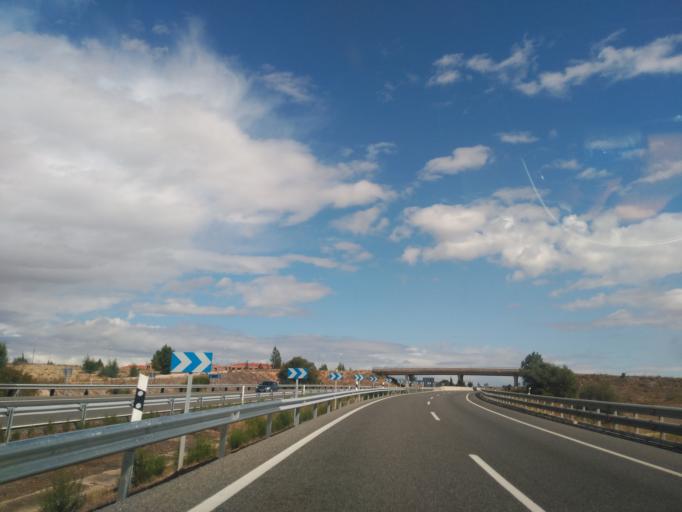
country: ES
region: Castille and Leon
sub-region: Provincia de Burgos
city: Buniel
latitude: 42.3106
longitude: -3.8152
